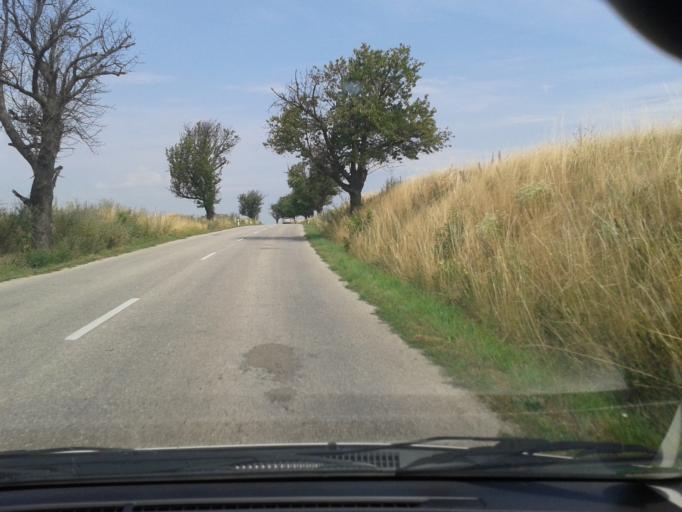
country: HU
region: Komarom-Esztergom
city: Esztergom
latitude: 47.9067
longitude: 18.7547
